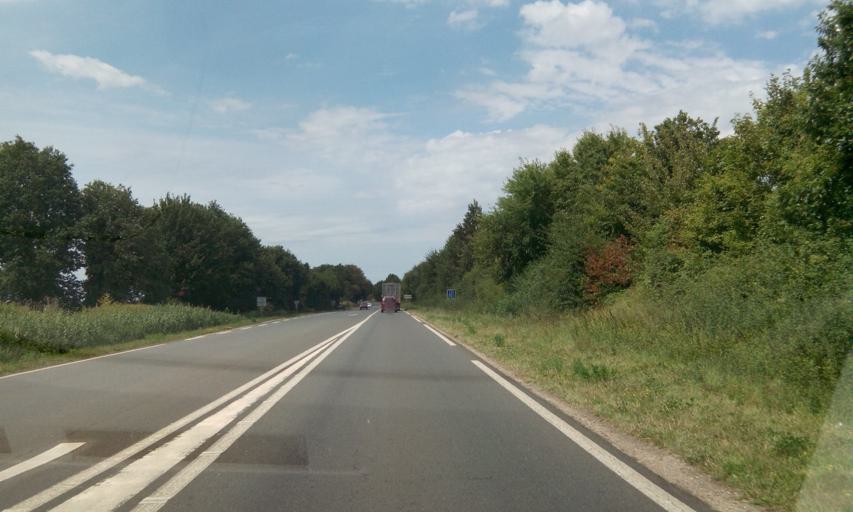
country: FR
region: Poitou-Charentes
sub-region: Departement des Deux-Sevres
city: Celles-sur-Belle
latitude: 46.2532
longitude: -0.2022
